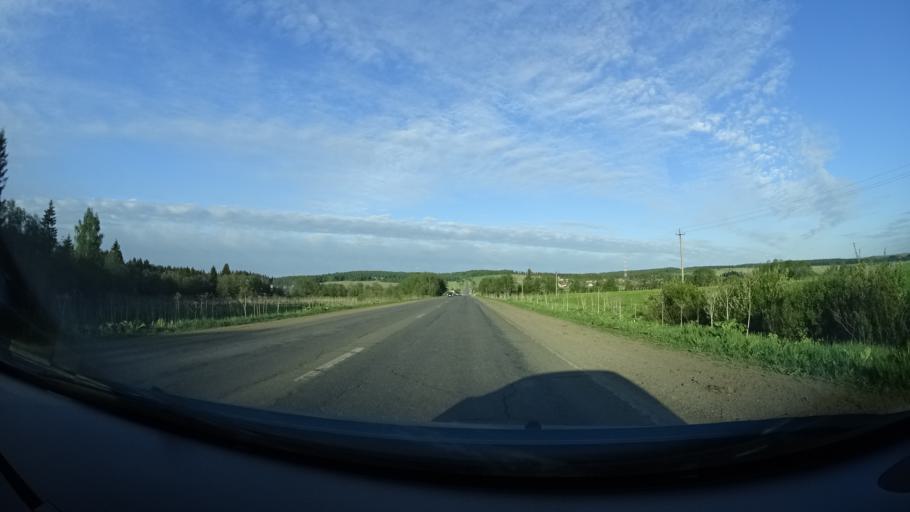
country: RU
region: Perm
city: Kultayevo
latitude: 57.8559
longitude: 55.8585
